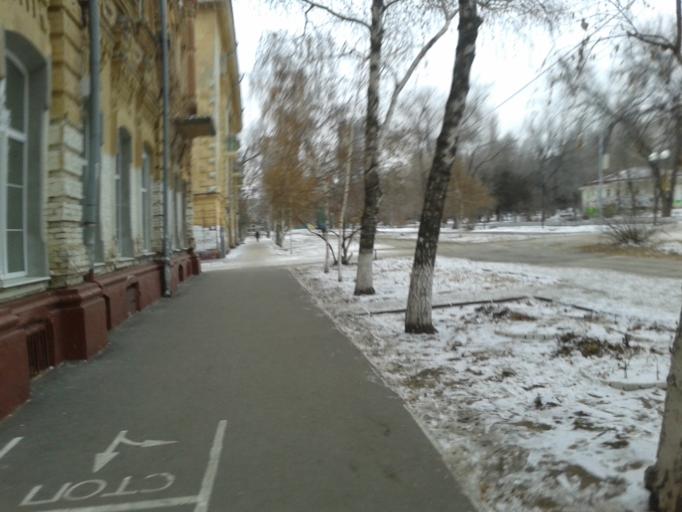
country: RU
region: Volgograd
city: Volgograd
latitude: 48.7071
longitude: 44.5106
